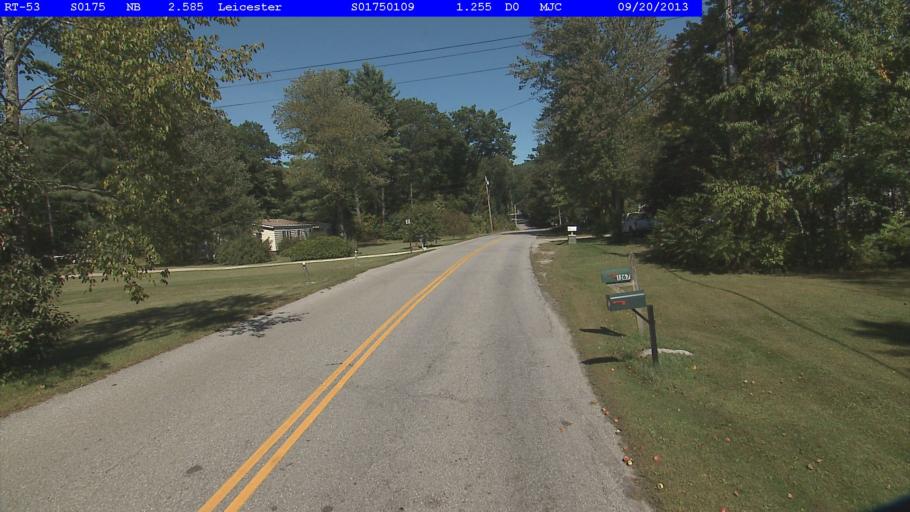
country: US
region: Vermont
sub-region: Rutland County
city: Brandon
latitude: 43.8612
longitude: -73.0679
